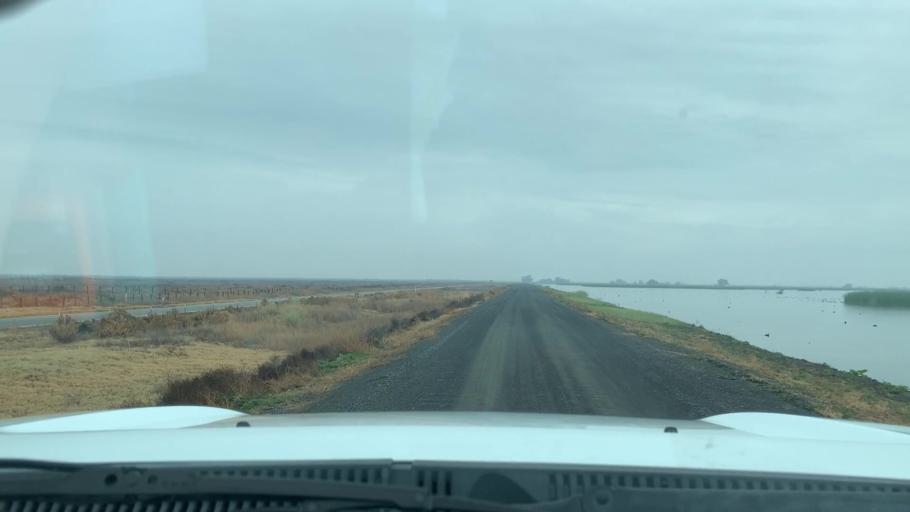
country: US
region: California
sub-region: Tulare County
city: Alpaugh
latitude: 35.7475
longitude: -119.5799
